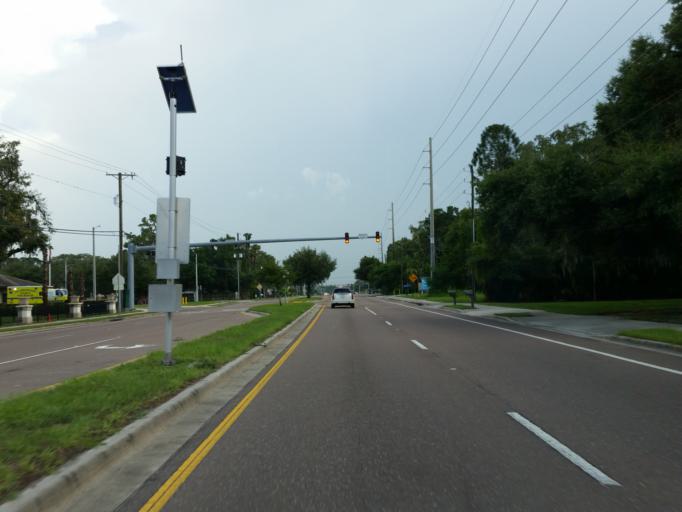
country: US
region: Florida
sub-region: Hillsborough County
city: Riverview
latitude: 27.8977
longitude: -82.3187
